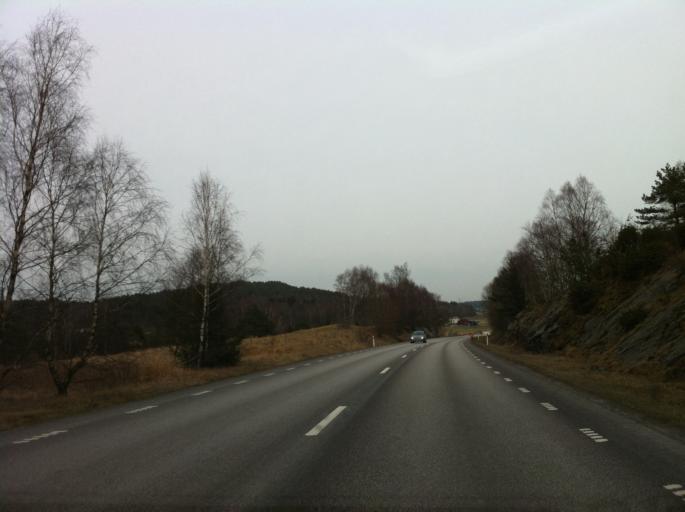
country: SE
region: Vaestra Goetaland
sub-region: Tjorns Kommun
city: Myggenas
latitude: 58.0061
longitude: 11.6699
